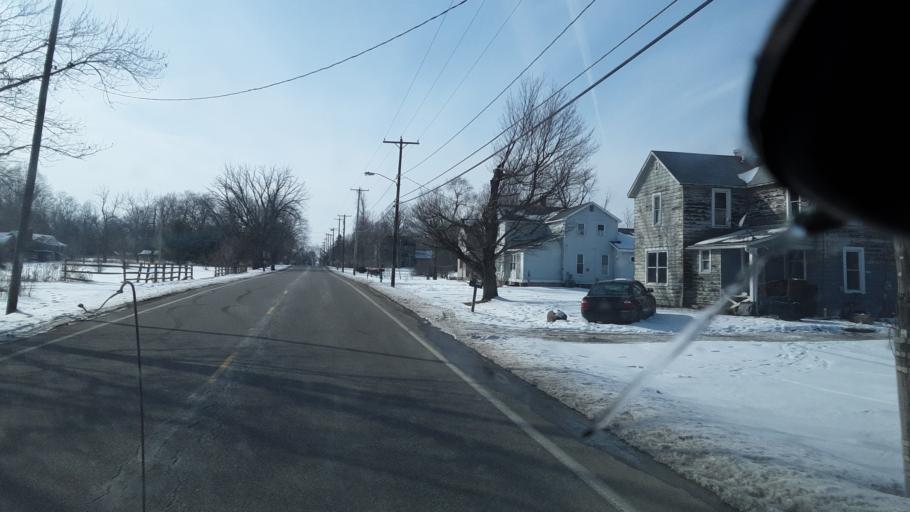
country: US
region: Ohio
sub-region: Mahoning County
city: Sebring
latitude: 41.0248
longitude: -81.0421
